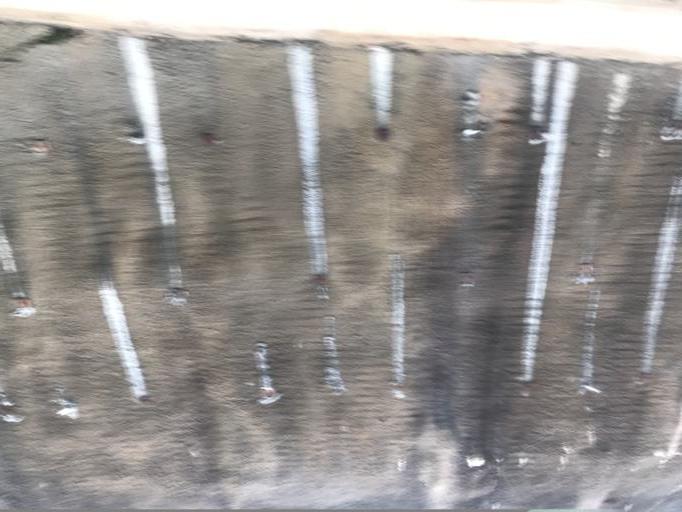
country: TR
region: Bartin
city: Amasra
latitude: 41.7180
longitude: 32.3956
